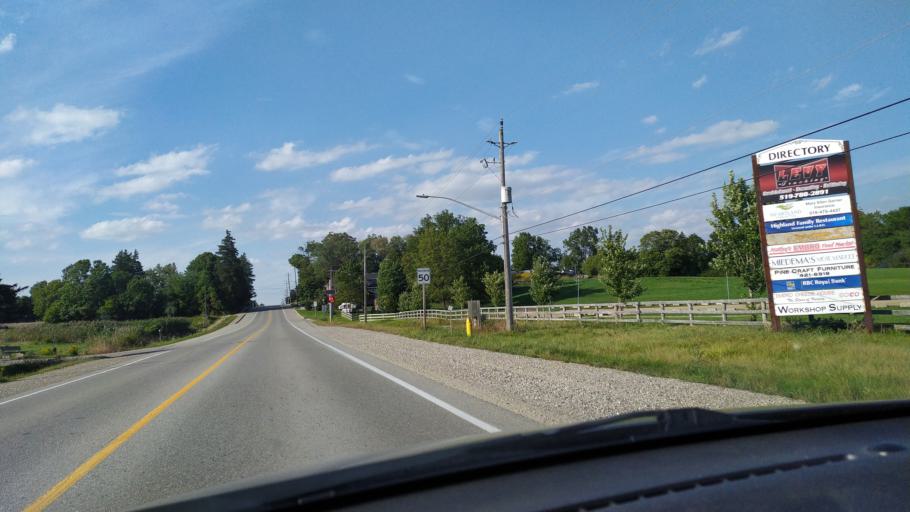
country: CA
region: Ontario
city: Ingersoll
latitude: 43.1509
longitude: -80.8986
